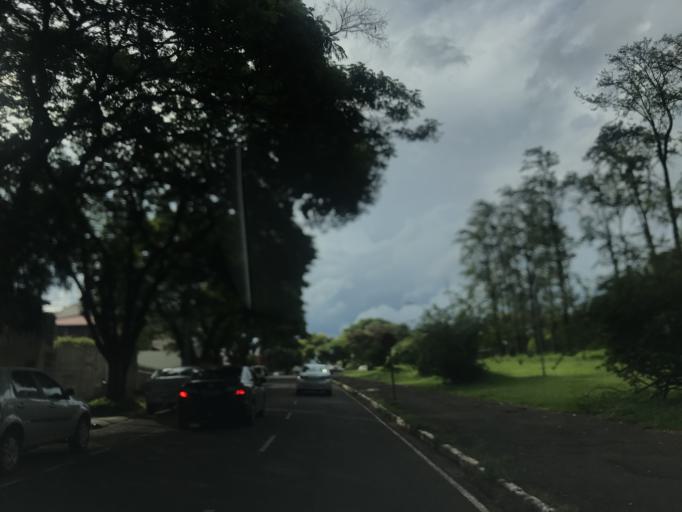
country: BR
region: Parana
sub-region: Maringa
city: Maringa
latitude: -23.4274
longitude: -51.9633
